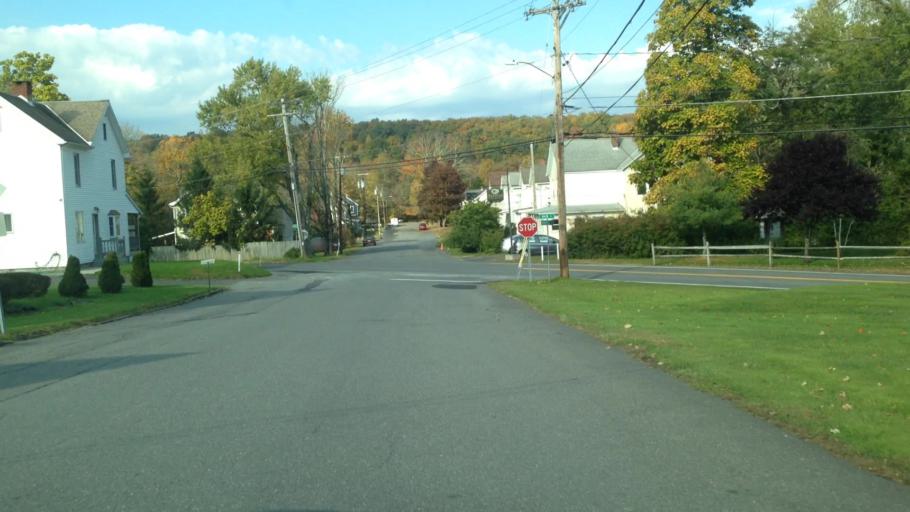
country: US
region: New York
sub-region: Ulster County
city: Tillson
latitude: 41.8380
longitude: -74.0398
